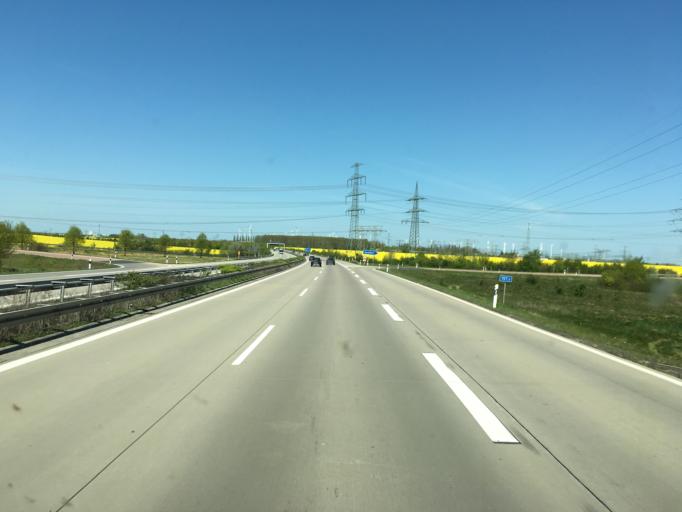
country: DE
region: Saxony-Anhalt
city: Bad Lauchstadt
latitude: 51.3943
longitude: 11.9015
